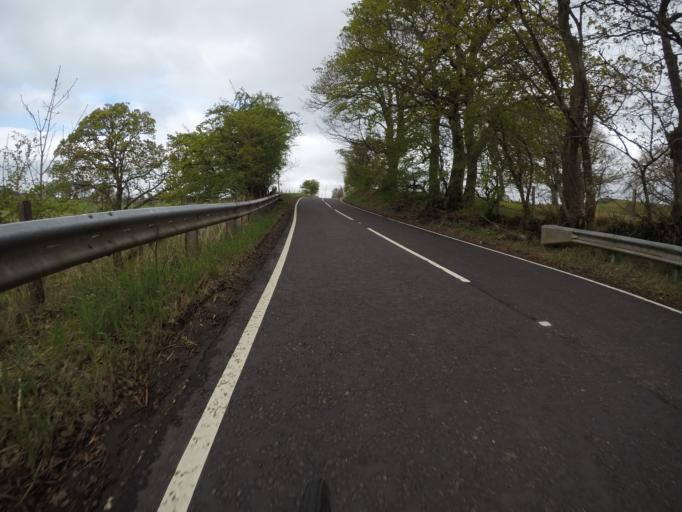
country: GB
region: Scotland
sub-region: East Renfrewshire
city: Barrhead
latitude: 55.7515
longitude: -4.3884
